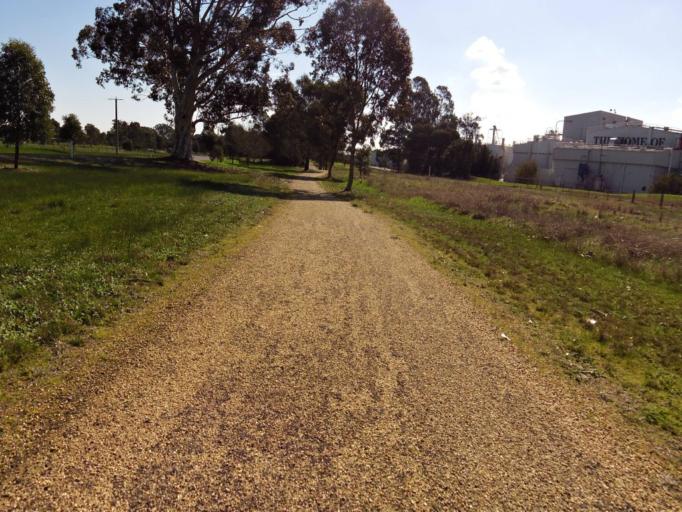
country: AU
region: New South Wales
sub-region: Corowa Shire
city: Corowa
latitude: -36.0144
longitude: 146.4108
